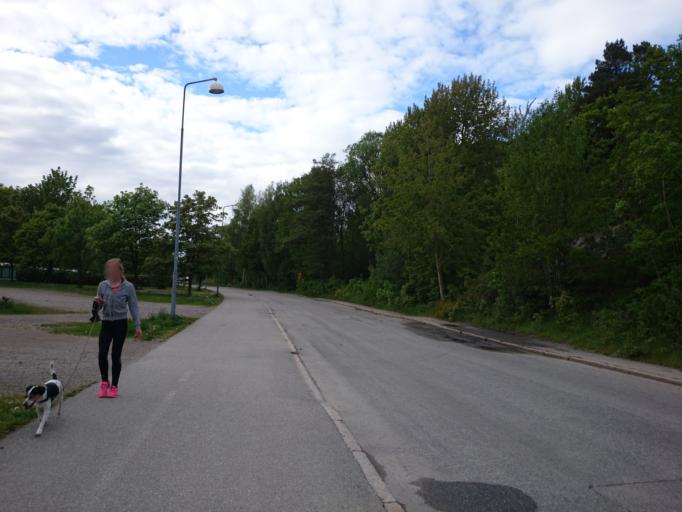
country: SE
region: Stockholm
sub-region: Nynashamns Kommun
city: Nynashamn
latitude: 58.8963
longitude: 17.9336
